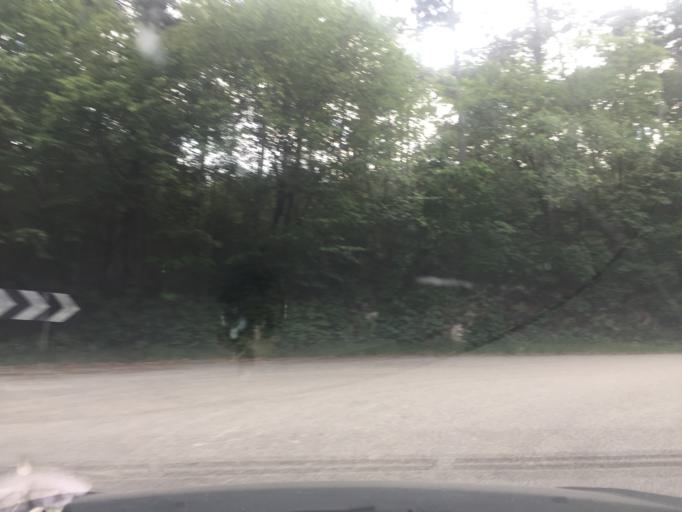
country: IT
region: Friuli Venezia Giulia
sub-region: Provincia di Gorizia
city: Savogna d'Isonzo
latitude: 45.8904
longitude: 13.5645
